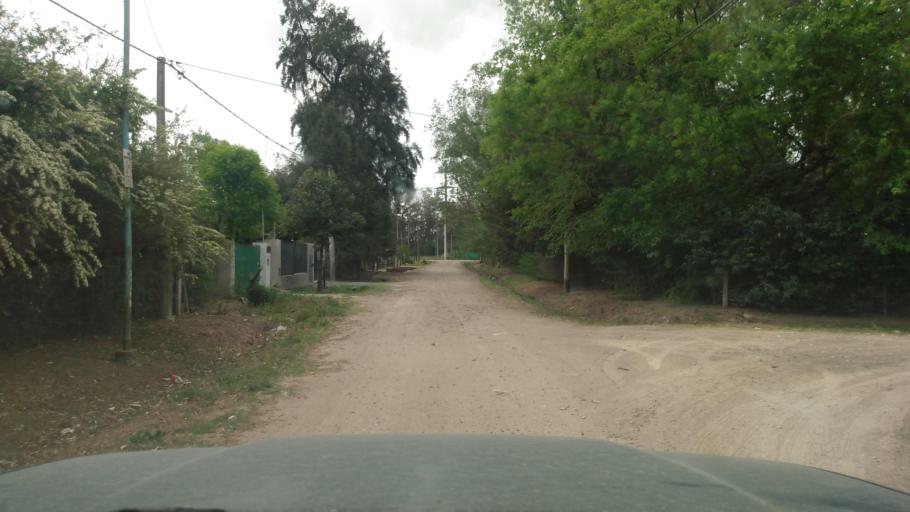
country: AR
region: Buenos Aires
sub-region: Partido de Lujan
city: Lujan
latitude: -34.5879
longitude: -59.1328
